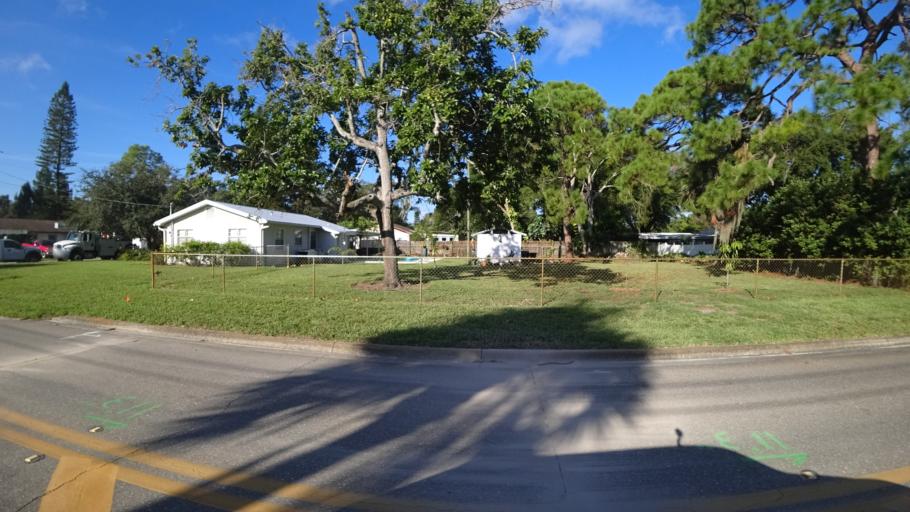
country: US
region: Florida
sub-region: Manatee County
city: West Bradenton
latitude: 27.4914
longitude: -82.5998
